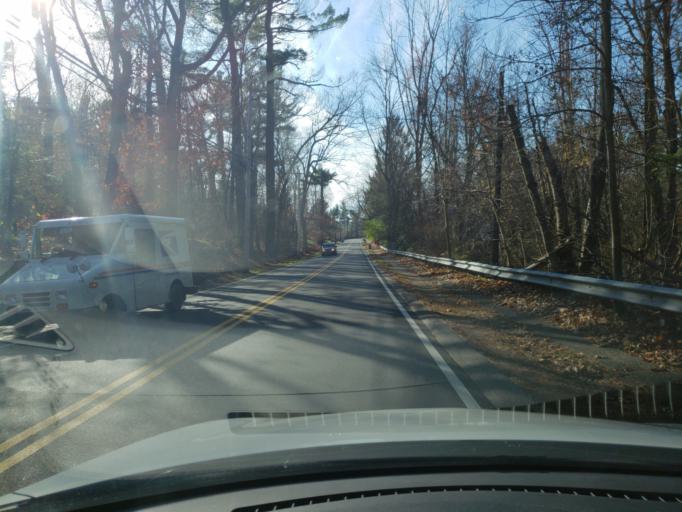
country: US
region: Massachusetts
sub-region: Essex County
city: Andover
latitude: 42.6463
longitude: -71.1436
